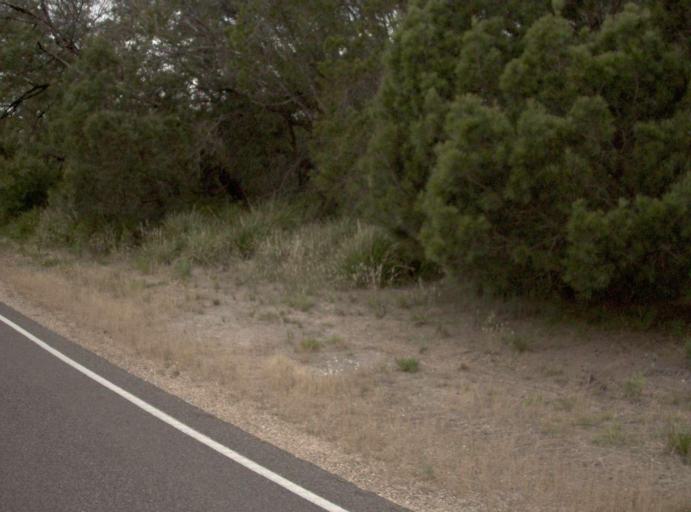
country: AU
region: Victoria
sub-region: East Gippsland
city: Bairnsdale
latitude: -37.9906
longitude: 147.3961
